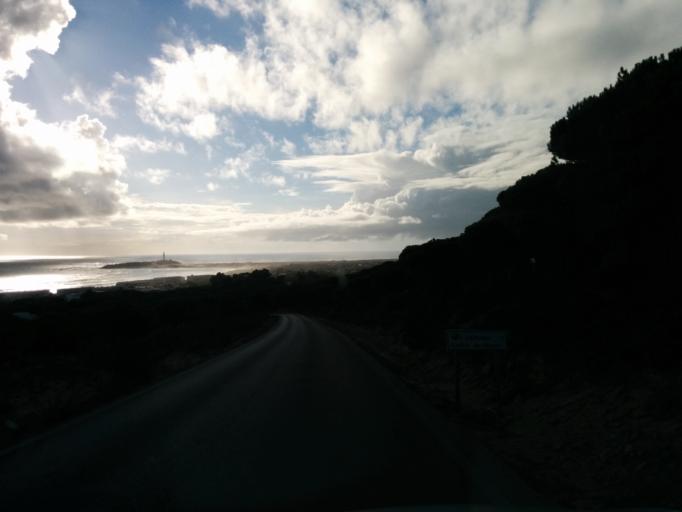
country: ES
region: Andalusia
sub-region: Provincia de Cadiz
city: Vejer de la Frontera
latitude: 36.1883
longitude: -6.0066
